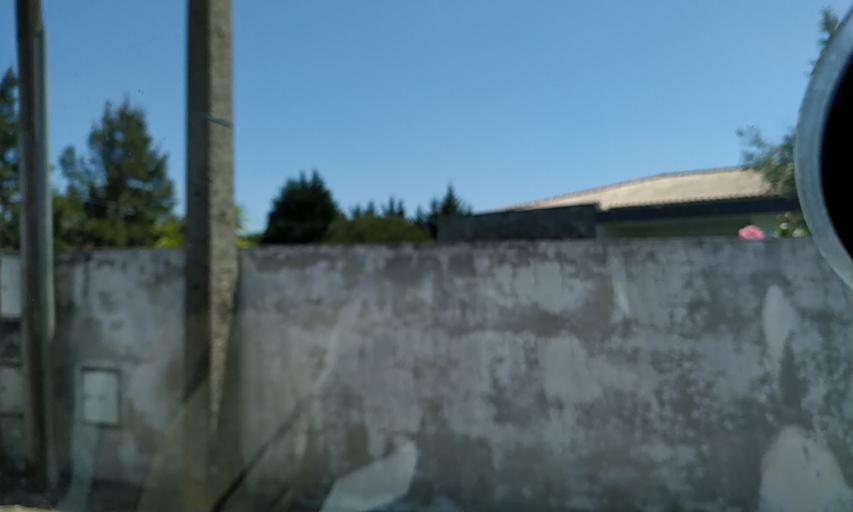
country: PT
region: Setubal
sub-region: Palmela
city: Palmela
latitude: 38.6038
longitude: -8.7859
